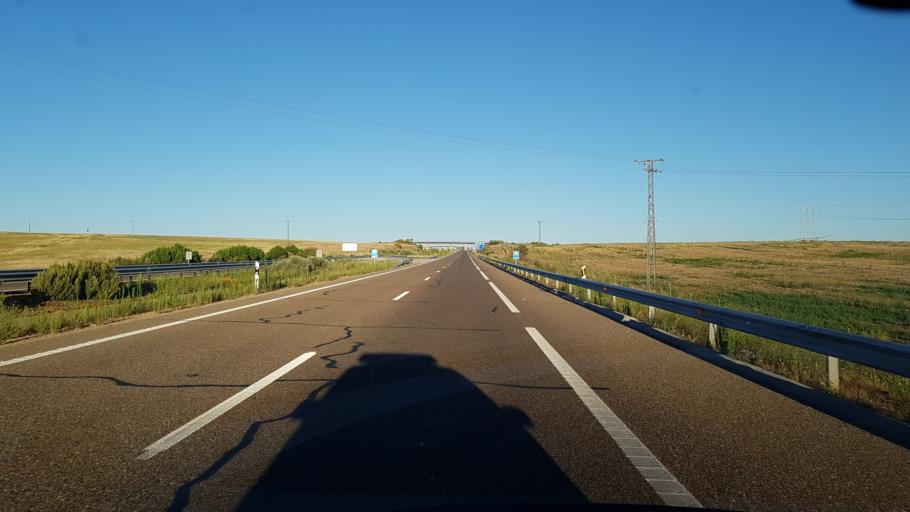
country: ES
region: Castille and Leon
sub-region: Provincia de Zamora
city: Matilla la Seca
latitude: 41.5678
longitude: -5.5064
